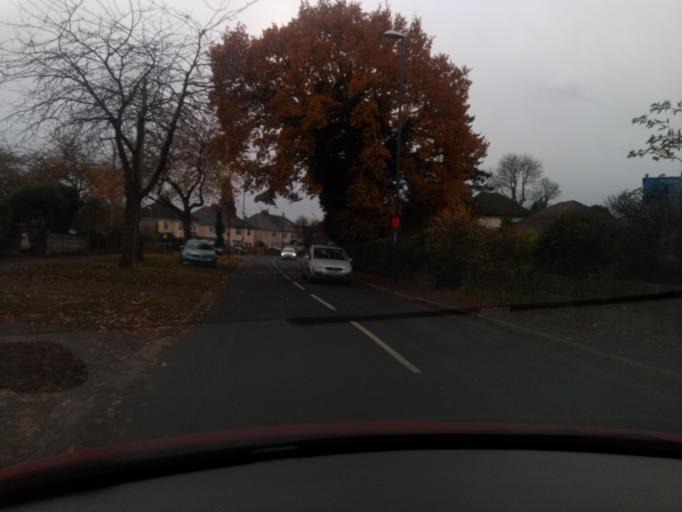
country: GB
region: England
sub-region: Derbyshire
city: Borrowash
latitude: 52.9353
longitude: -1.4243
